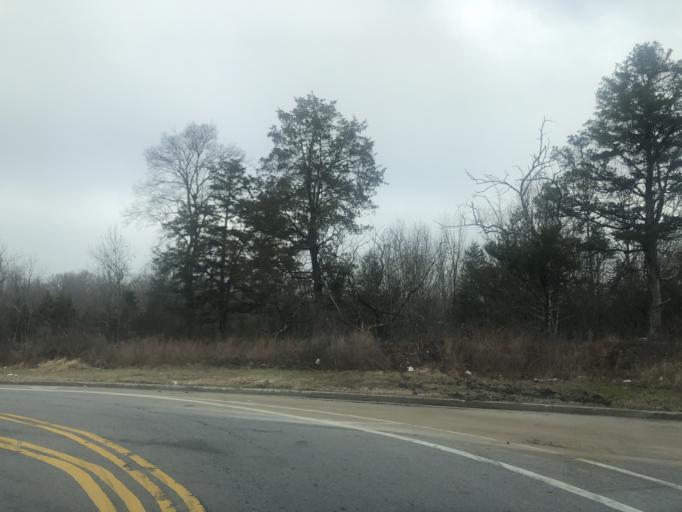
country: US
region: Tennessee
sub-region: Rutherford County
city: La Vergne
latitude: 36.0711
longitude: -86.6458
